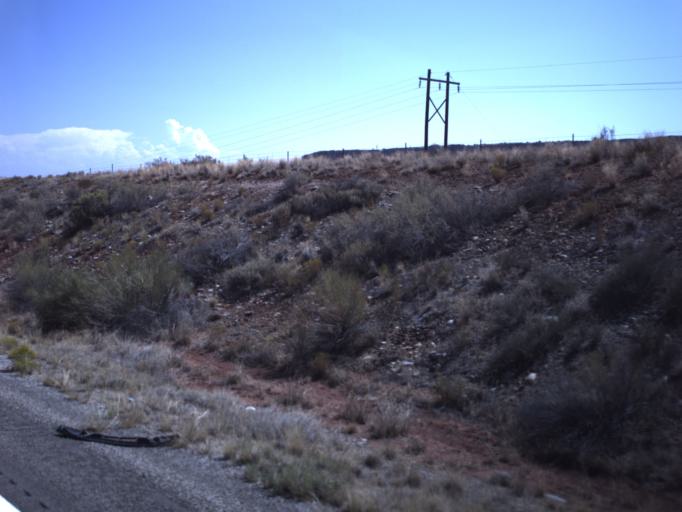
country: US
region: Utah
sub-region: San Juan County
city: Blanding
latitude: 37.2742
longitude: -109.5906
